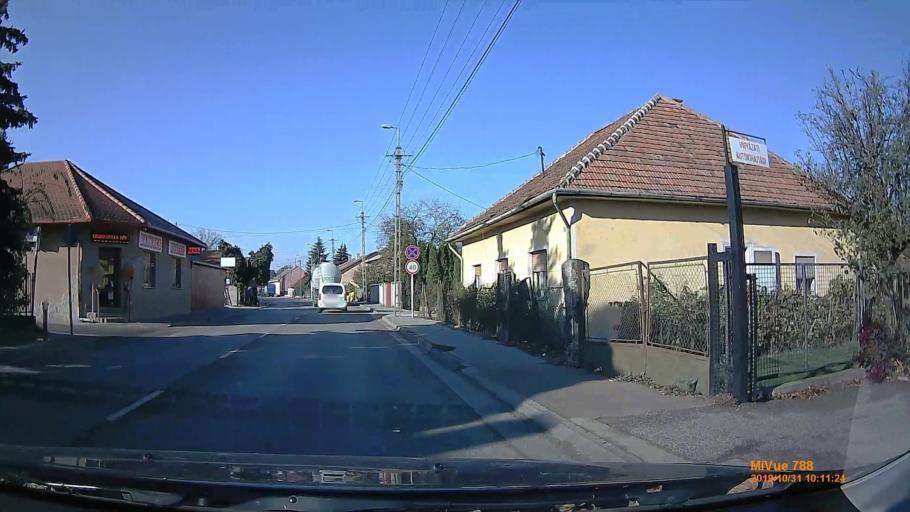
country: HU
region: Pest
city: Pecel
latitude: 47.4909
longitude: 19.3405
